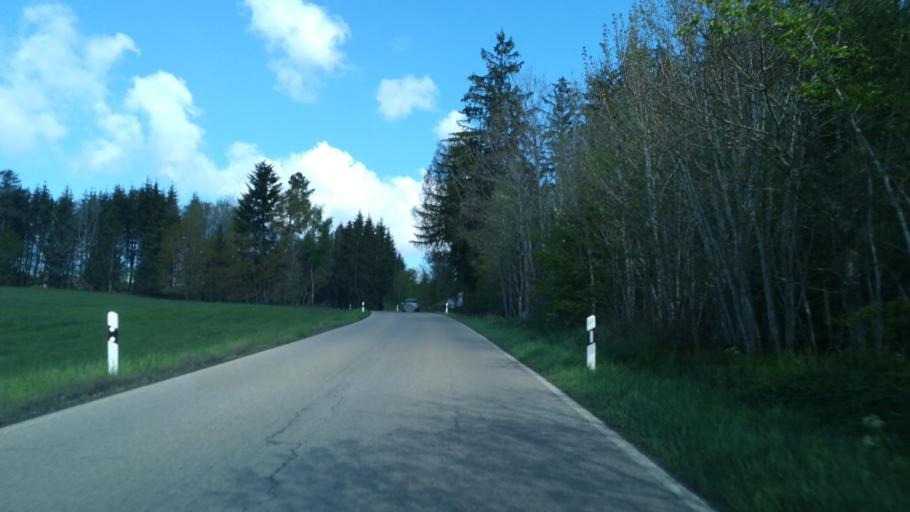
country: DE
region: Baden-Wuerttemberg
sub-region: Freiburg Region
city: Grafenhausen
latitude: 47.7571
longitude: 8.3021
